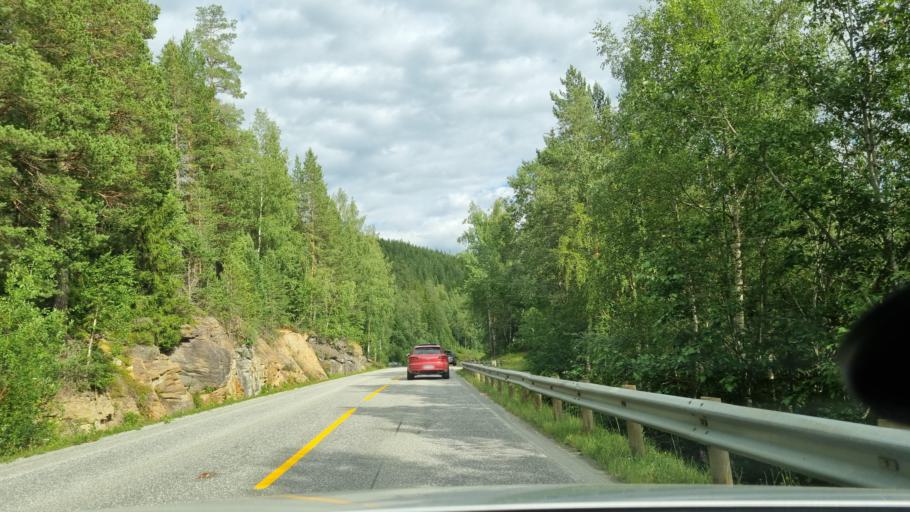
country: NO
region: Sor-Trondelag
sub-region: Selbu
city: Mebonden
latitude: 62.9659
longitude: 10.9657
